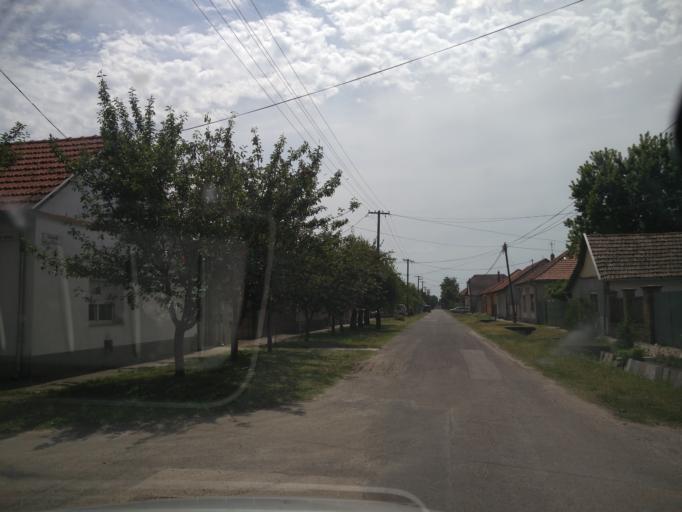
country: HU
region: Csongrad
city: Sandorfalva
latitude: 46.3698
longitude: 20.1041
